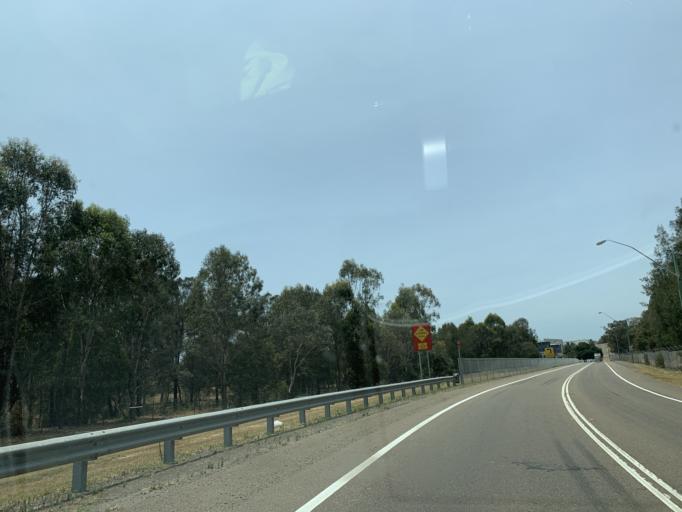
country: AU
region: New South Wales
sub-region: Blacktown
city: Doonside
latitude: -33.8019
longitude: 150.8661
